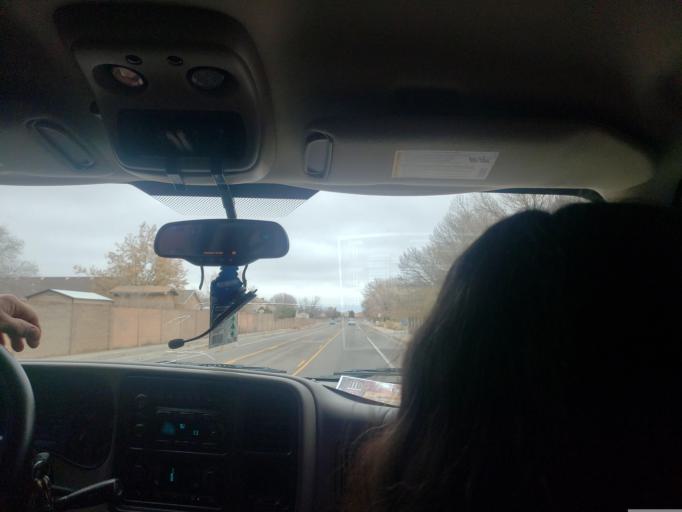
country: US
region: New Mexico
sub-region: Bernalillo County
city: Albuquerque
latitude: 35.0906
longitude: -106.7162
